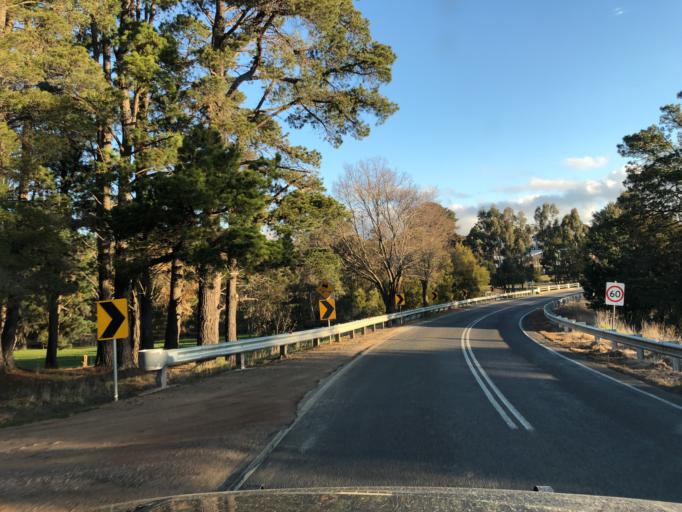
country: AU
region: Victoria
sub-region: Moorabool
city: Bacchus Marsh
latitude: -37.5977
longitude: 144.2312
